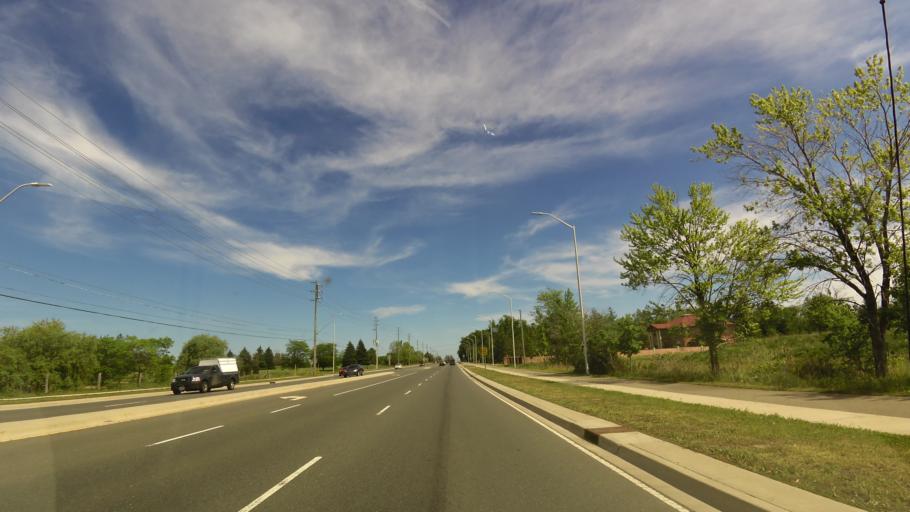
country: CA
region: Ontario
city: Oakville
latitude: 43.4198
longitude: -79.7544
